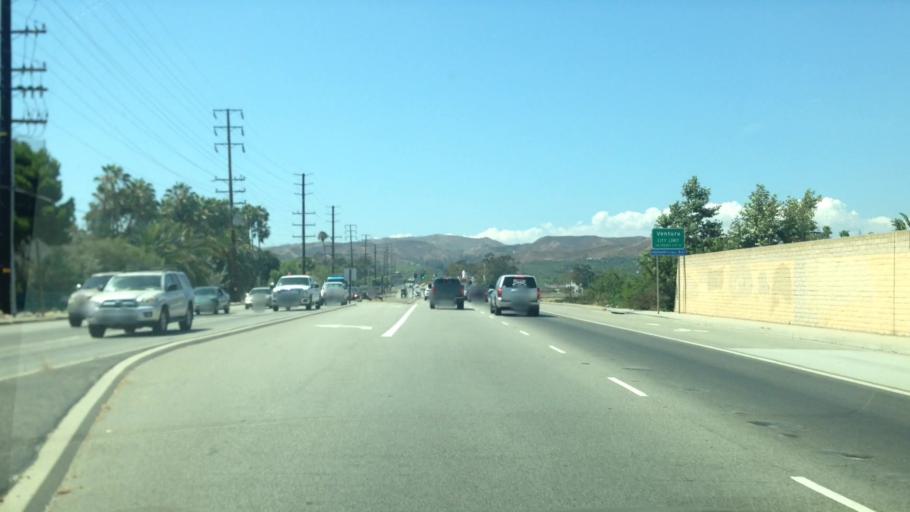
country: US
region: California
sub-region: Ventura County
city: Saticoy
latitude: 34.2845
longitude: -119.1517
